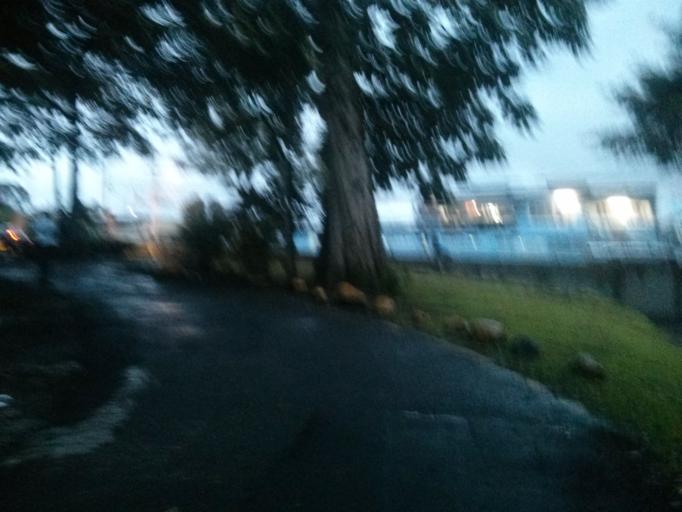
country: CR
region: San Jose
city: San Pedro
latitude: 9.9350
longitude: -84.0540
